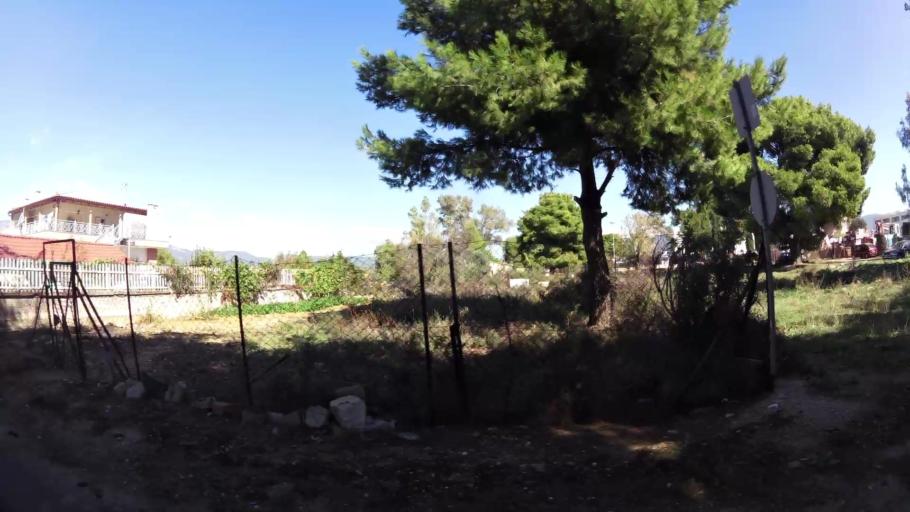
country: GR
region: Attica
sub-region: Nomarchia Athinas
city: Lykovrysi
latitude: 38.0882
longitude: 23.7792
